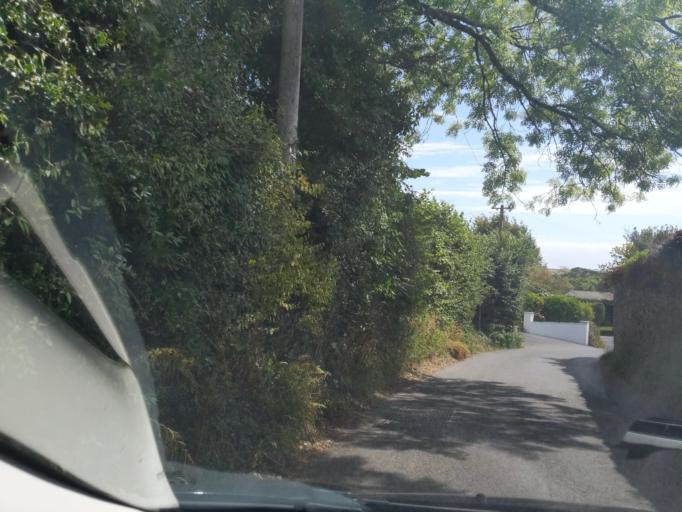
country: GB
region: England
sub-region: Devon
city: Modbury
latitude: 50.3550
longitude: -3.8877
